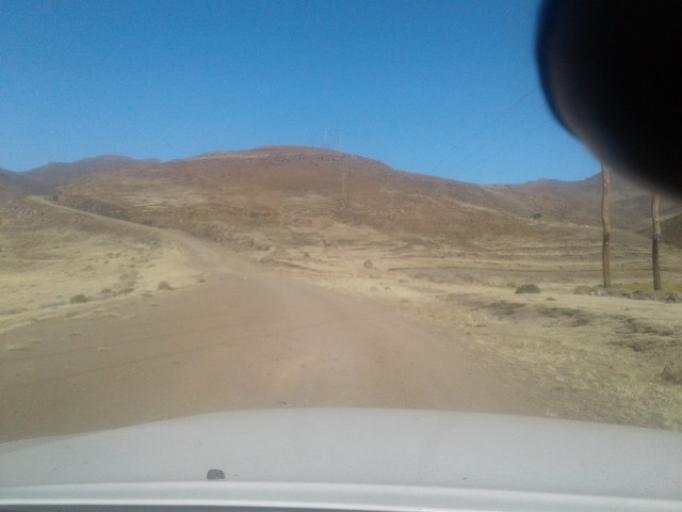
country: LS
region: Maseru
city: Nako
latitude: -29.3864
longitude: 28.0069
